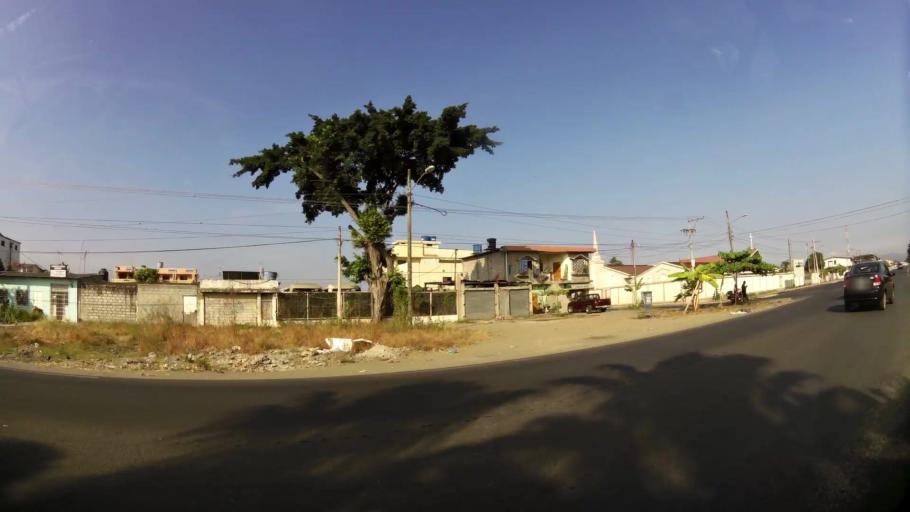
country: EC
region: Guayas
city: Eloy Alfaro
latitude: -2.1807
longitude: -79.8404
